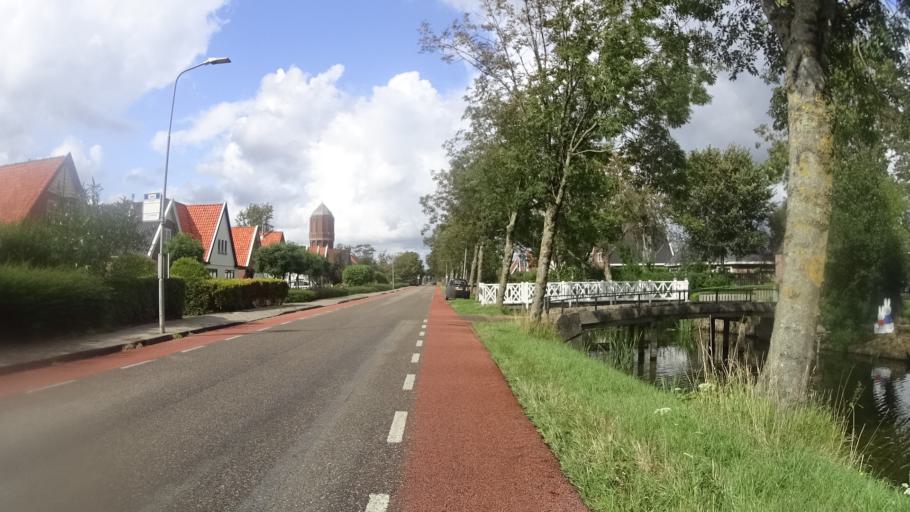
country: NL
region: North Holland
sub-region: Gemeente Schagen
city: Schagen
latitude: 52.8376
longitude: 4.8606
